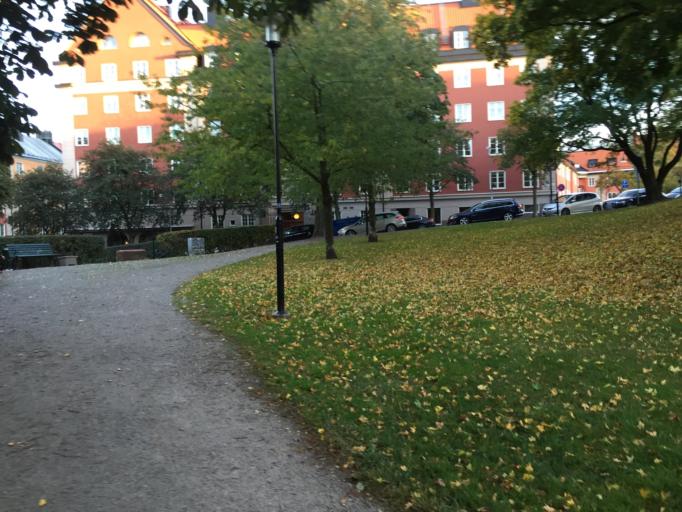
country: SE
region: Stockholm
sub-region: Stockholms Kommun
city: Stockholm
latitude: 59.3442
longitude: 18.0343
